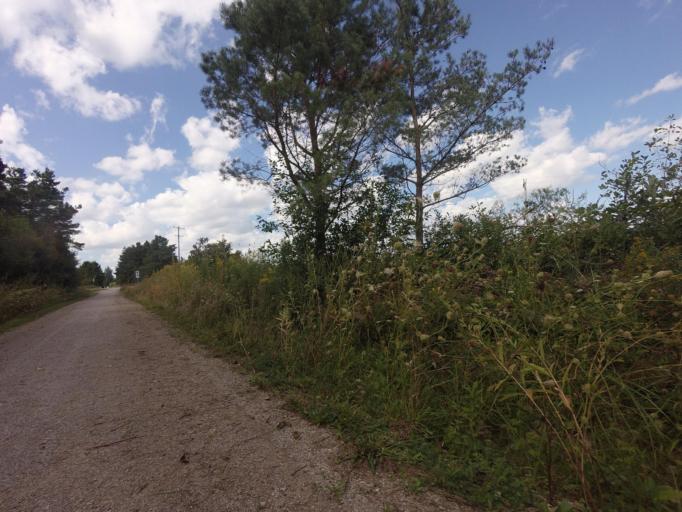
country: CA
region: Ontario
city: Huron East
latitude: 43.7292
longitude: -81.4129
